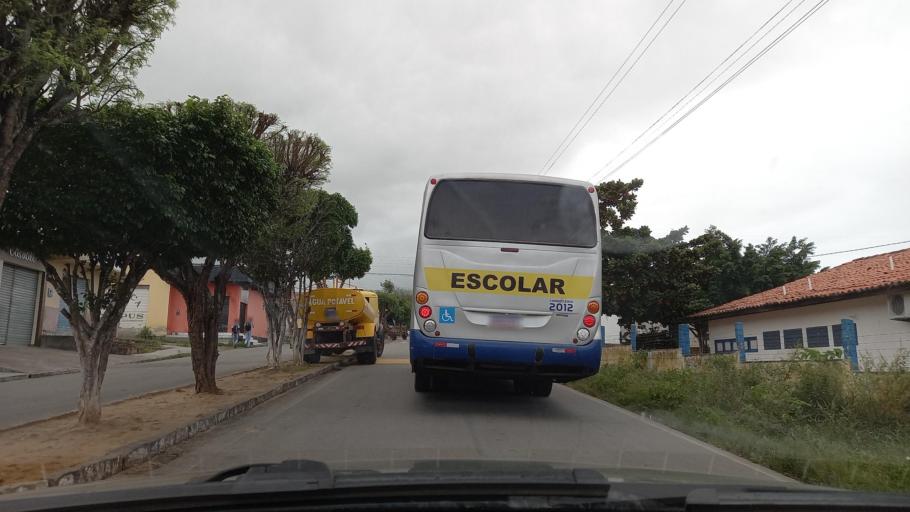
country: BR
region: Sergipe
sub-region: Caninde De Sao Francisco
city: Caninde de Sao Francisco
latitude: -9.6055
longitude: -37.7586
